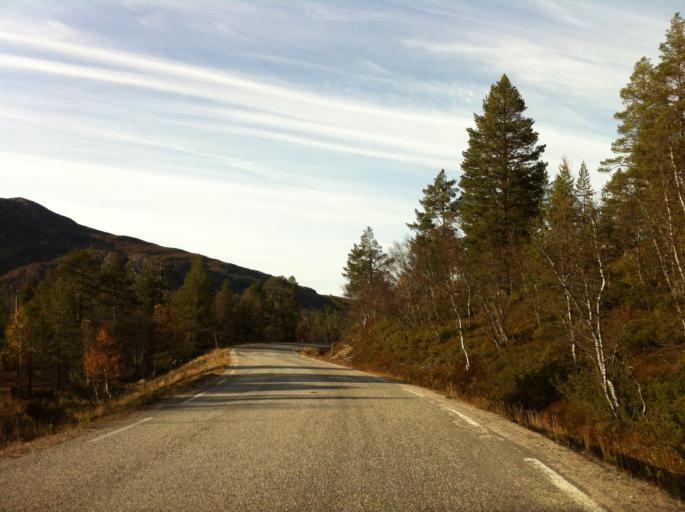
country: NO
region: Hedmark
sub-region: Engerdal
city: Engerdal
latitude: 62.0904
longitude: 12.0471
